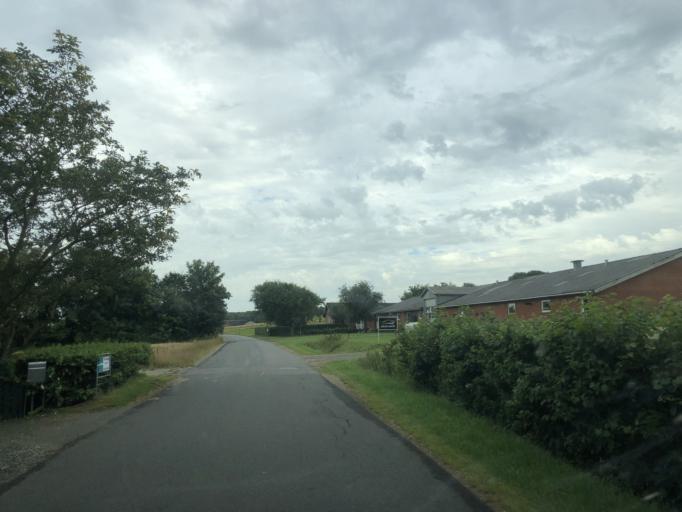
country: DK
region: Central Jutland
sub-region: Holstebro Kommune
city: Holstebro
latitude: 56.3898
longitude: 8.5261
